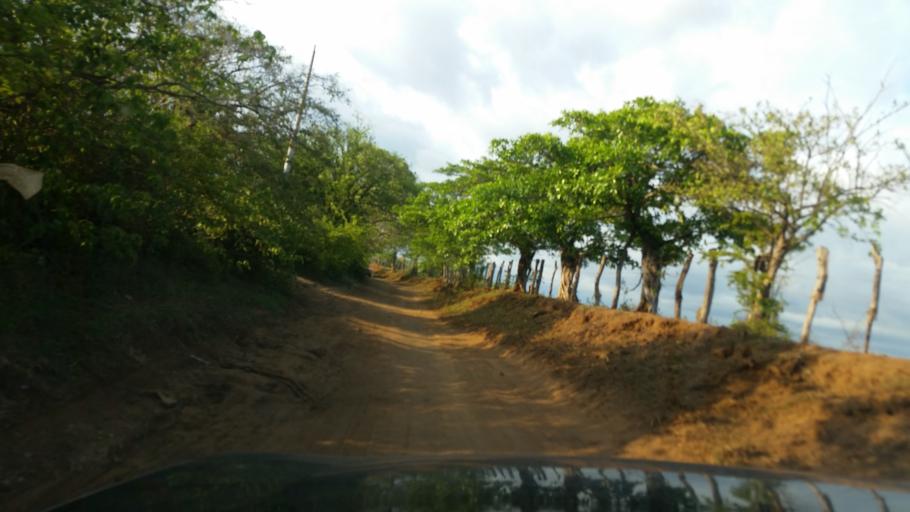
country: NI
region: Managua
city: Masachapa
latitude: 11.7909
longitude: -86.4703
